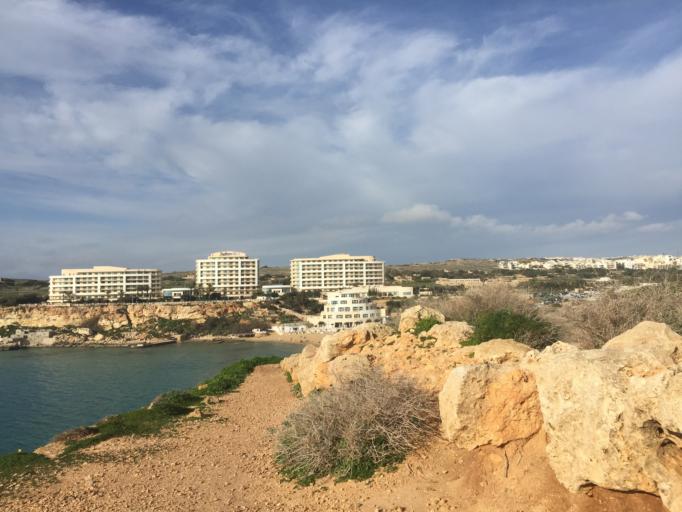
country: MT
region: L-Imgarr
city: Imgarr
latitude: 35.9313
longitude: 14.3433
